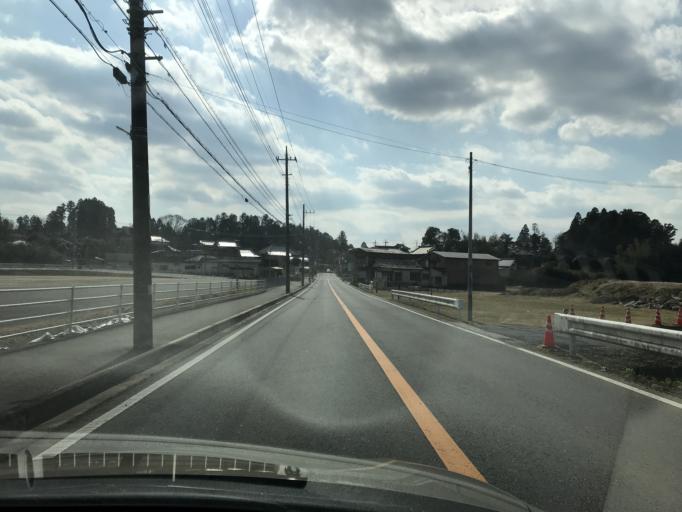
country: JP
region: Chiba
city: Sawara
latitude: 35.8158
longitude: 140.5051
